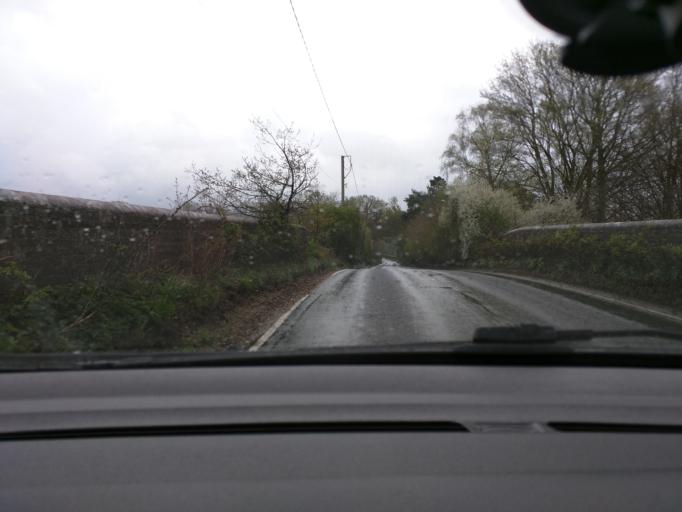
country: GB
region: England
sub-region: Suffolk
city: Saxmundham
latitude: 52.1871
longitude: 1.4791
